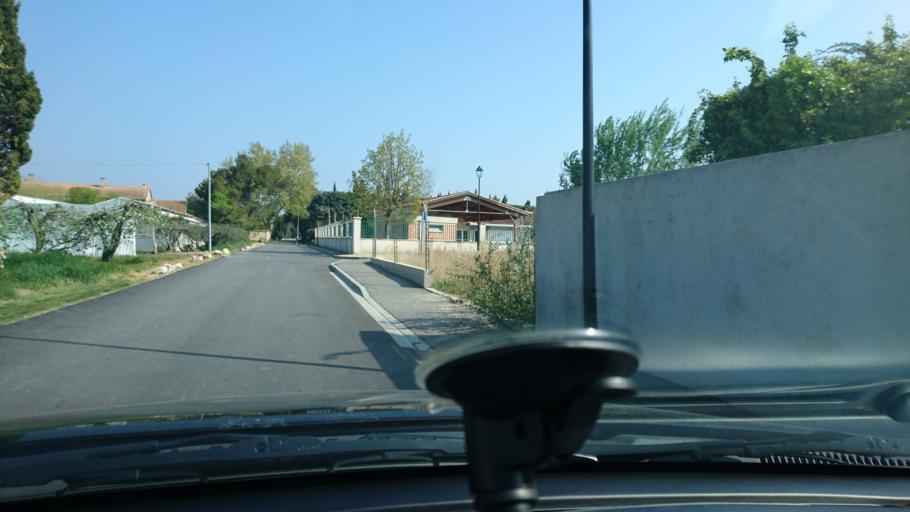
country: FR
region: Provence-Alpes-Cote d'Azur
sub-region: Departement des Bouches-du-Rhone
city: Saint-Andiol
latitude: 43.8334
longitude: 4.9005
